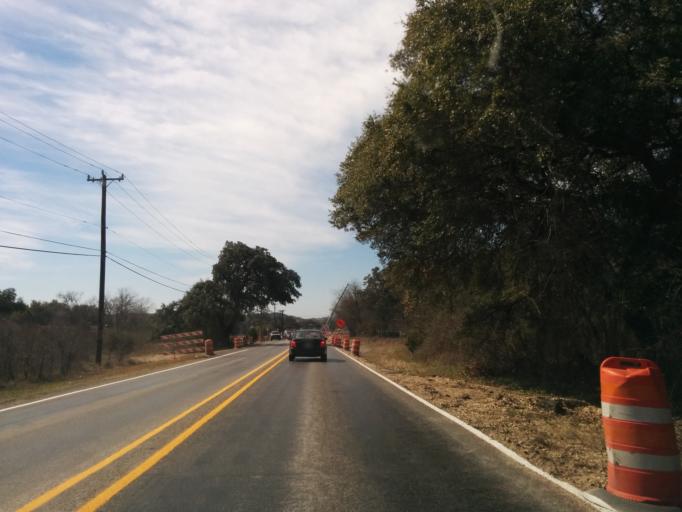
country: US
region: Texas
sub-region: Bexar County
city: Cross Mountain
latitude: 29.6784
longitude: -98.6328
